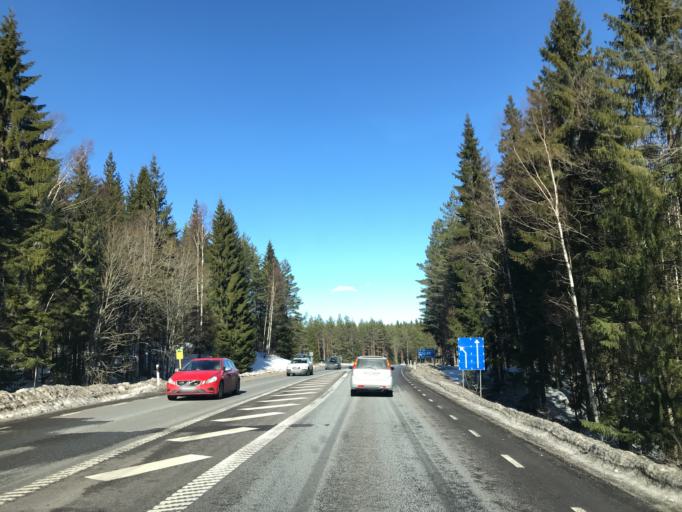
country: SE
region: Vaermland
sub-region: Filipstads Kommun
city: Filipstad
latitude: 59.7680
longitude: 14.2593
